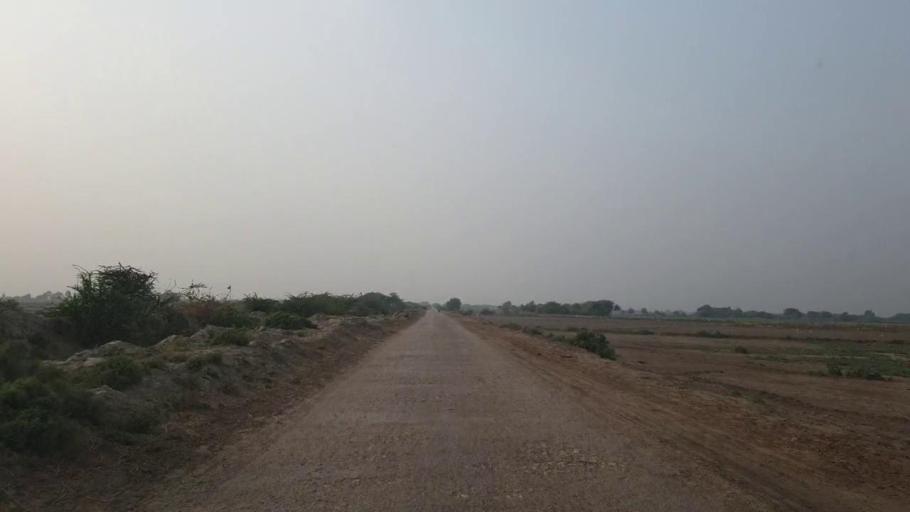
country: PK
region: Sindh
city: Mirpur Batoro
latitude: 24.6432
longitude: 68.3951
